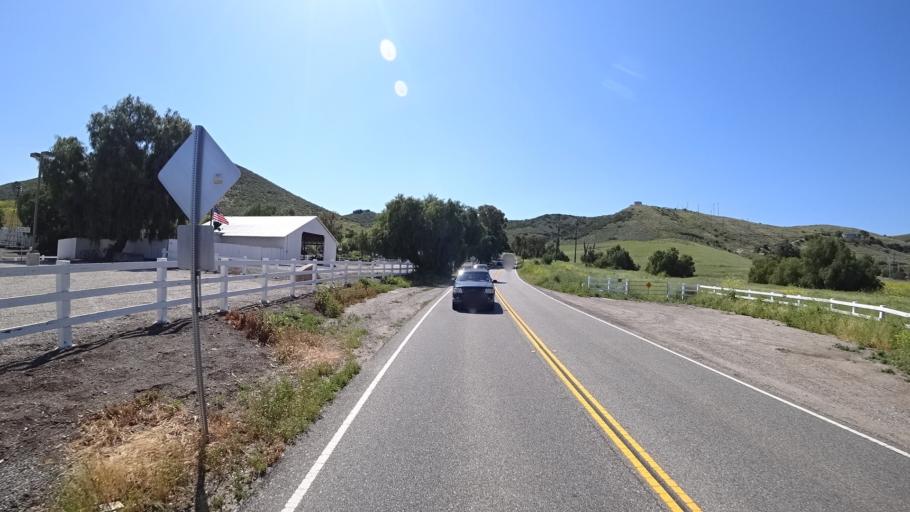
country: US
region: California
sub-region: Ventura County
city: Moorpark
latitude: 34.2439
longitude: -118.8633
